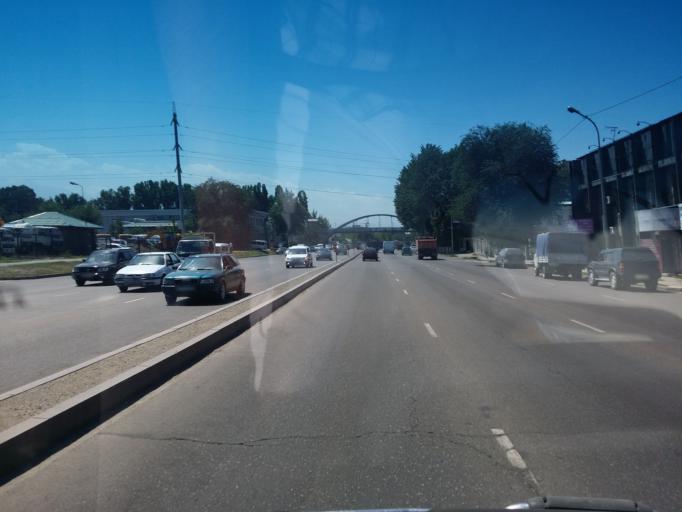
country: KZ
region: Almaty Qalasy
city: Almaty
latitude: 43.2835
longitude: 76.9179
